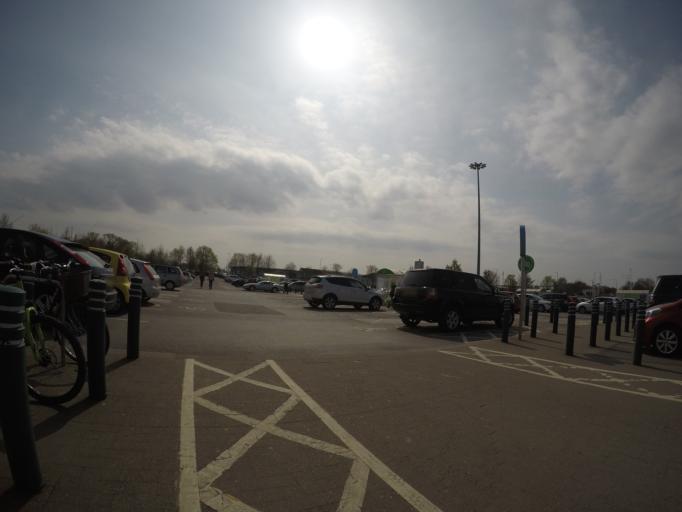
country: GB
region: England
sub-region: City of York
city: Huntington
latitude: 53.9861
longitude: -1.0443
